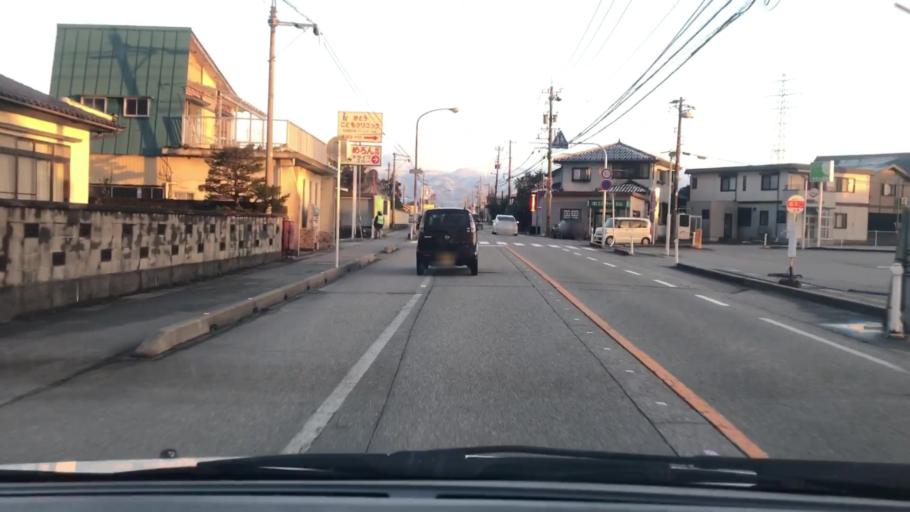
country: JP
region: Toyama
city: Kamiichi
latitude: 36.6680
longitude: 137.2944
